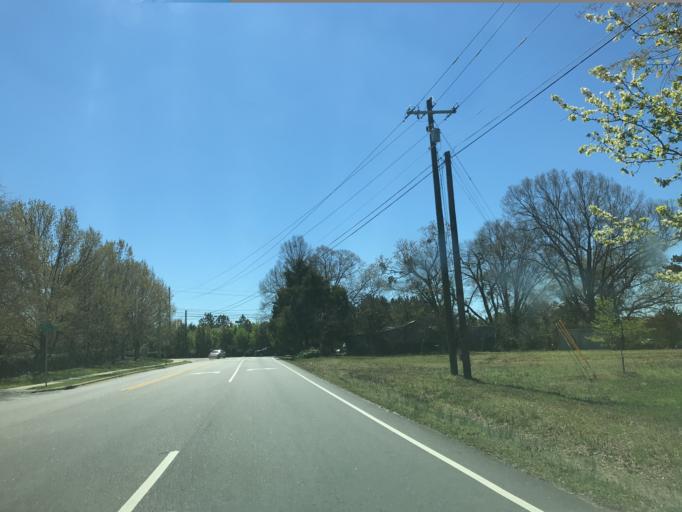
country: US
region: North Carolina
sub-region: Wake County
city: West Raleigh
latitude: 35.7499
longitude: -78.7179
